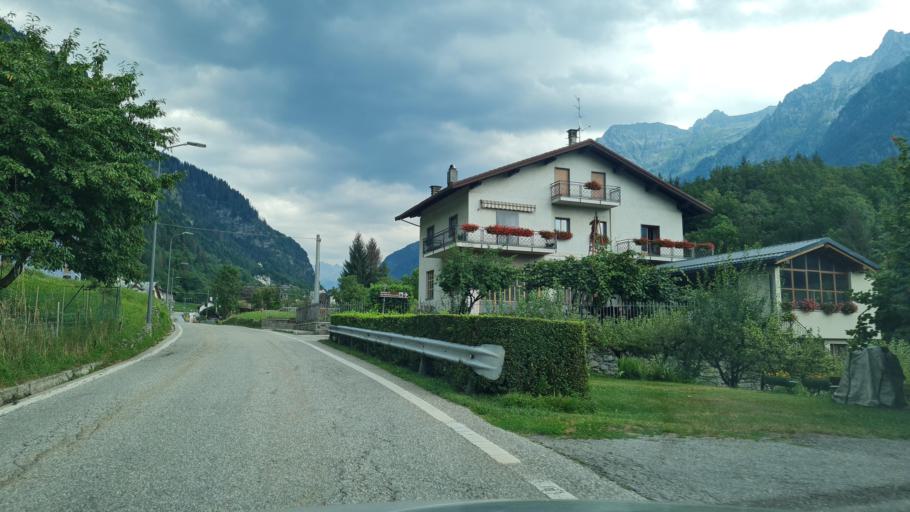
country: IT
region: Piedmont
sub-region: Provincia Verbano-Cusio-Ossola
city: Premia
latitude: 46.2632
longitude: 8.3310
